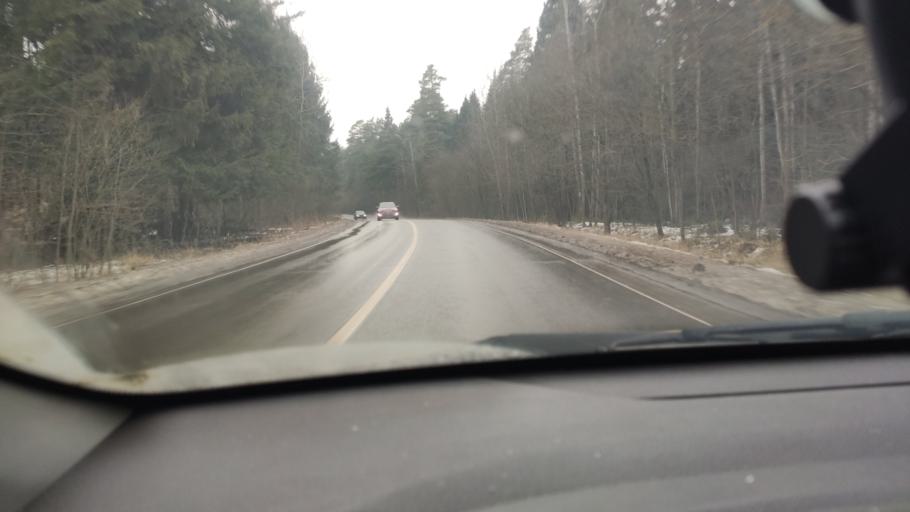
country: RU
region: Moskovskaya
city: Yakovlevskoye
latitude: 55.4551
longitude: 37.8866
